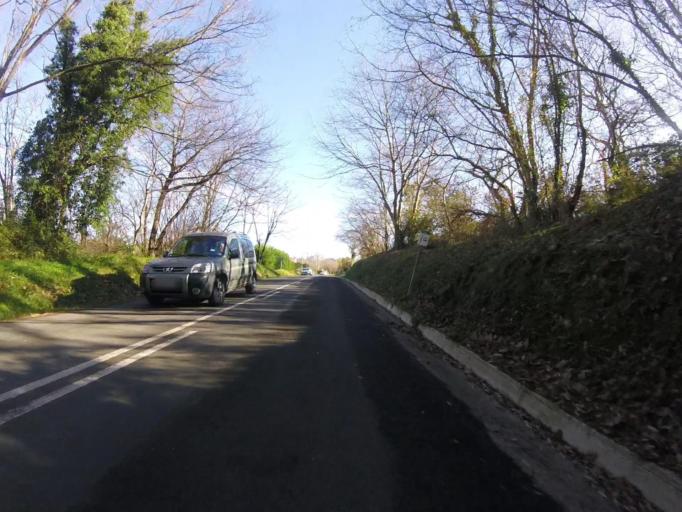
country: ES
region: Basque Country
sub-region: Provincia de Guipuzcoa
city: Fuenterrabia
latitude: 43.3671
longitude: -1.8233
